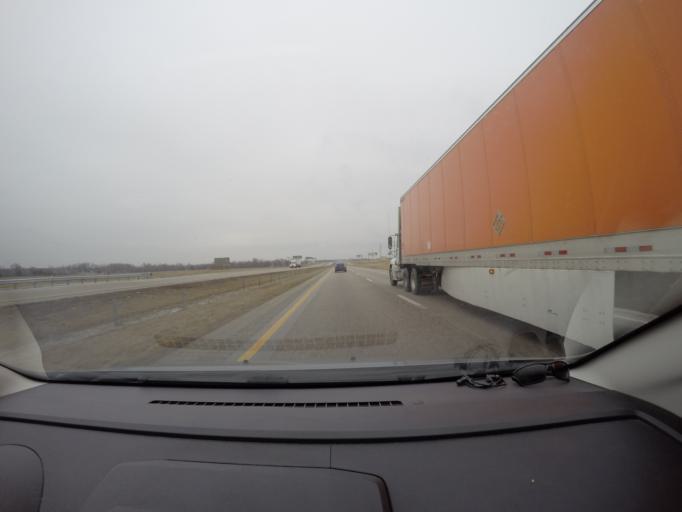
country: US
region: Missouri
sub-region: Montgomery County
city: Montgomery City
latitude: 38.8877
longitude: -91.4146
